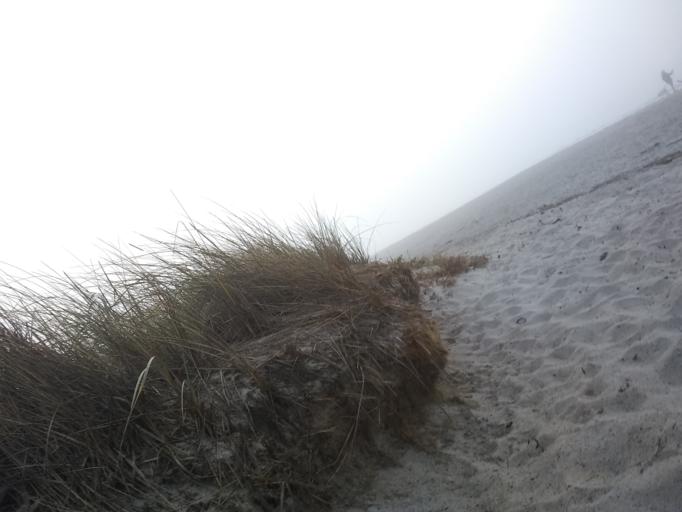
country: US
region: Maine
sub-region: Cumberland County
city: Scarborough
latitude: 43.5407
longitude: -70.3371
